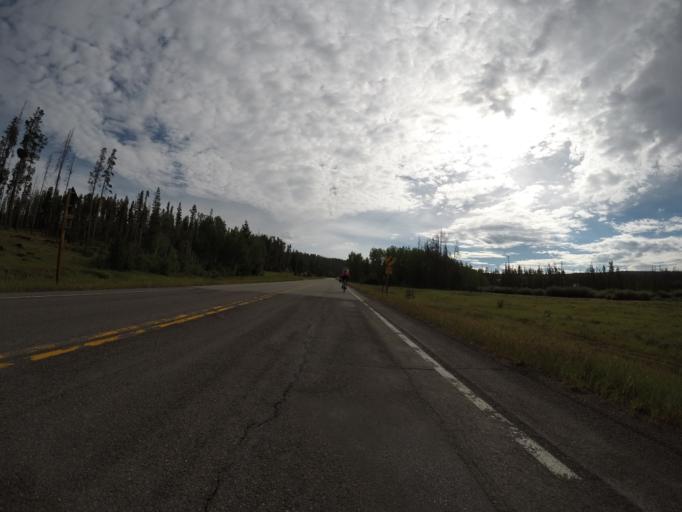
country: US
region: Wyoming
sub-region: Carbon County
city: Saratoga
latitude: 41.3248
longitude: -106.5009
